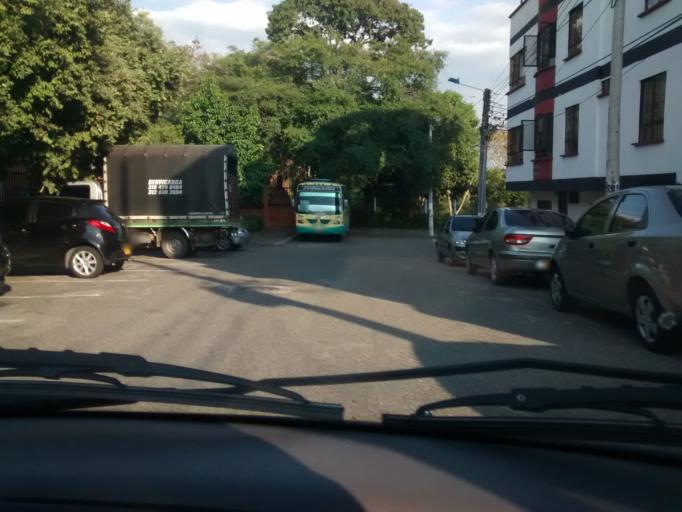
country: CO
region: Santander
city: Bucaramanga
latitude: 7.0962
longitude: -73.1335
